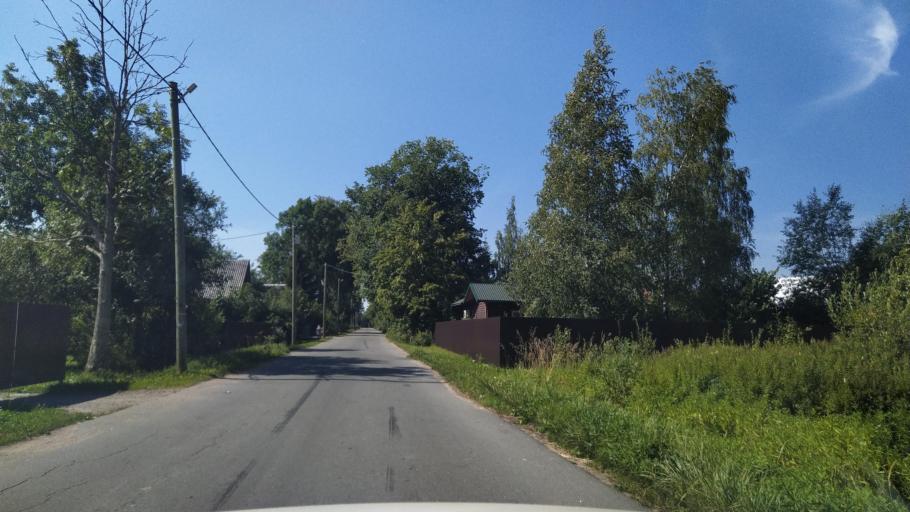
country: RU
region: Leningrad
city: Siverskiy
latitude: 59.2642
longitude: 30.0390
